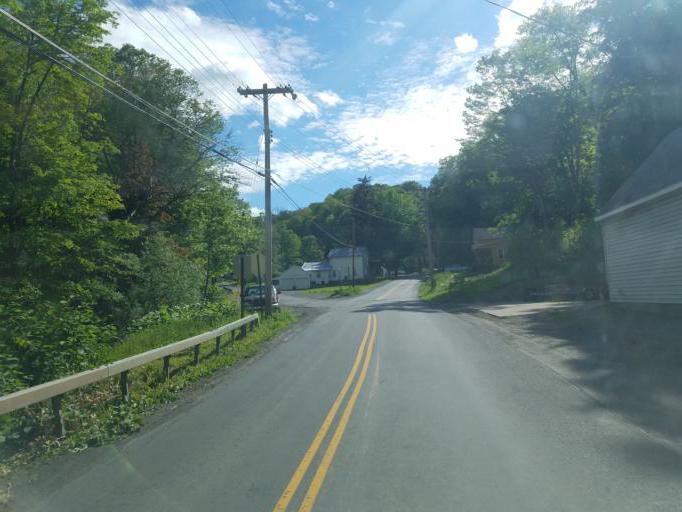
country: US
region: New York
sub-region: Herkimer County
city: Ilion
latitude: 42.9927
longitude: -75.0502
